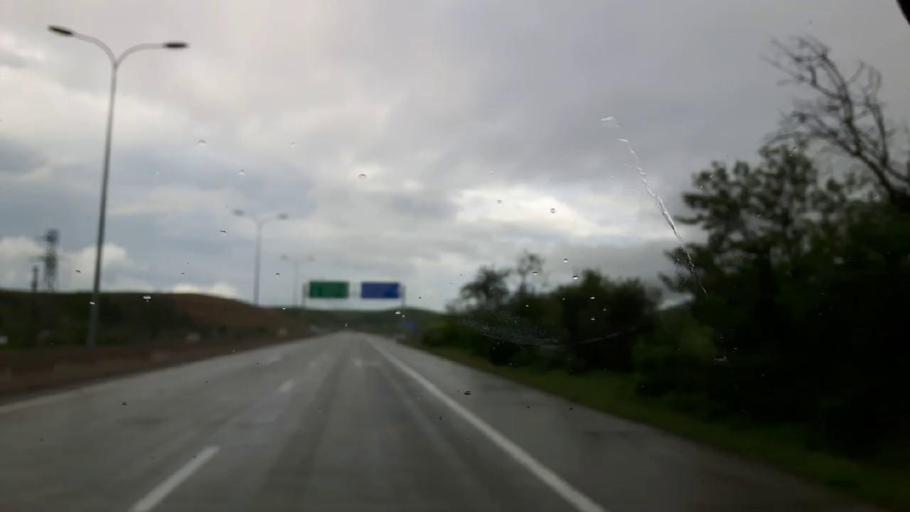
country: GE
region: Shida Kartli
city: Kaspi
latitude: 42.0002
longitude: 44.3879
